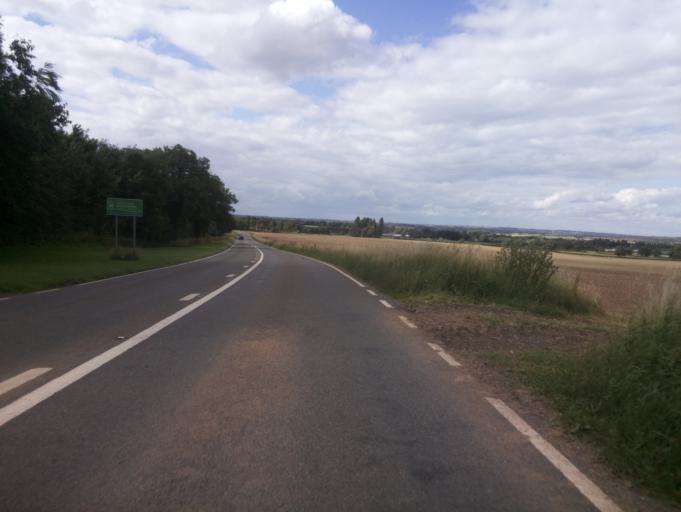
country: GB
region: England
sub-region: Leicestershire
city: Measham
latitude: 52.6677
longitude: -1.5386
